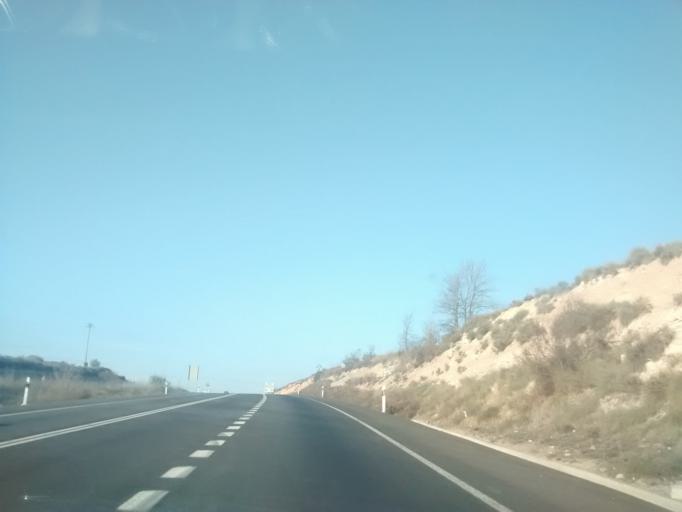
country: ES
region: Aragon
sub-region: Provincia de Huesca
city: Fraga
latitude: 41.5137
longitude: 0.2737
